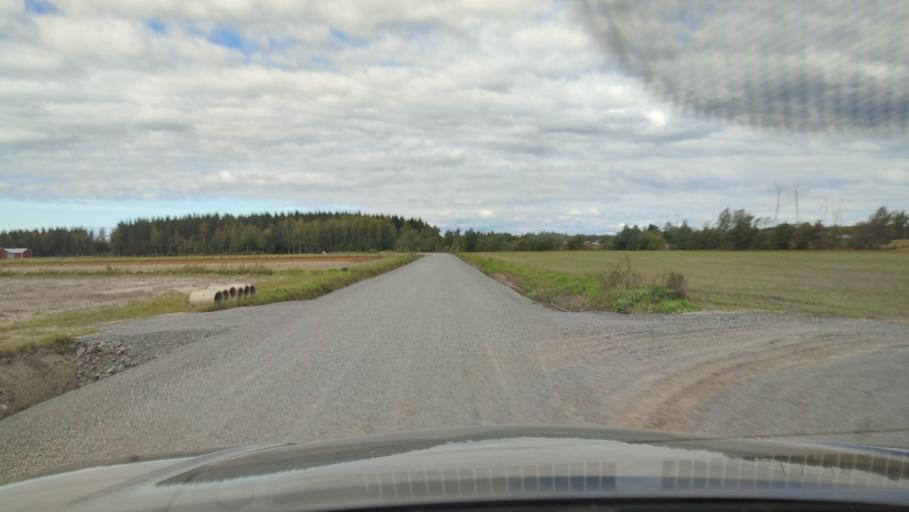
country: FI
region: Southern Ostrobothnia
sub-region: Suupohja
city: Karijoki
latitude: 62.2294
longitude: 21.6182
